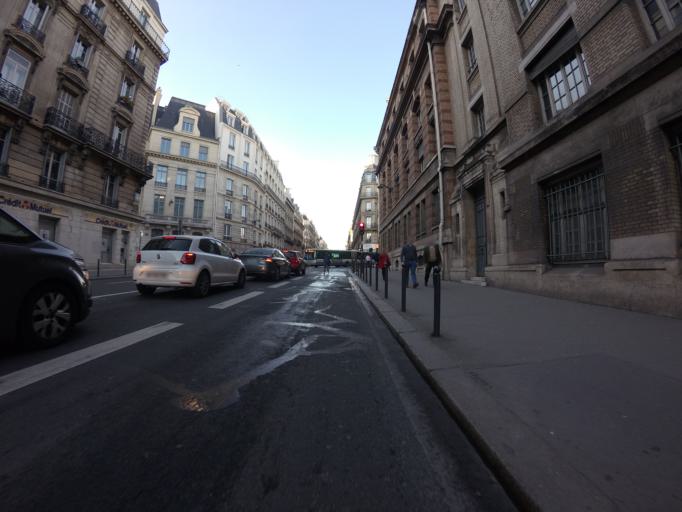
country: FR
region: Ile-de-France
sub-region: Paris
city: Saint-Ouen
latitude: 48.8782
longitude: 2.3229
